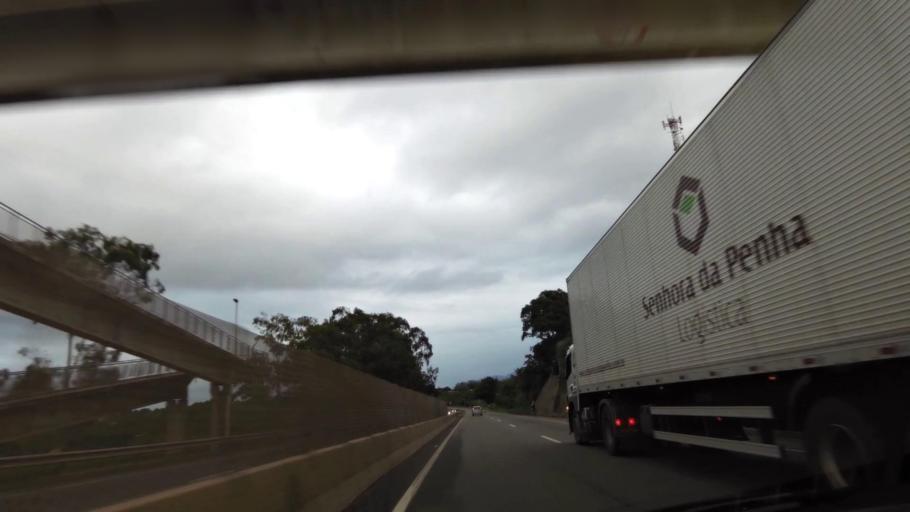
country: BR
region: Espirito Santo
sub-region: Viana
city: Viana
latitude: -20.4975
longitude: -40.3597
